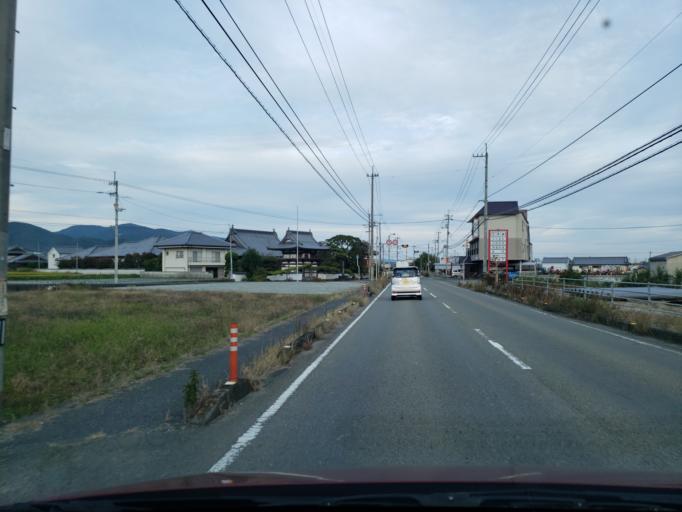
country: JP
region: Tokushima
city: Kamojimacho-jogejima
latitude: 34.0963
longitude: 134.3189
